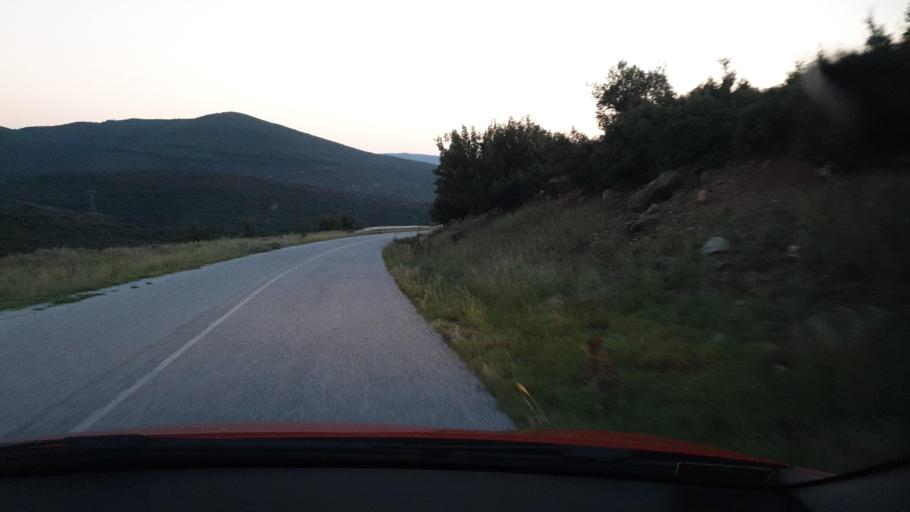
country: GR
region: Central Macedonia
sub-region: Nomos Thessalonikis
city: Peristera
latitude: 40.5129
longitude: 23.1685
